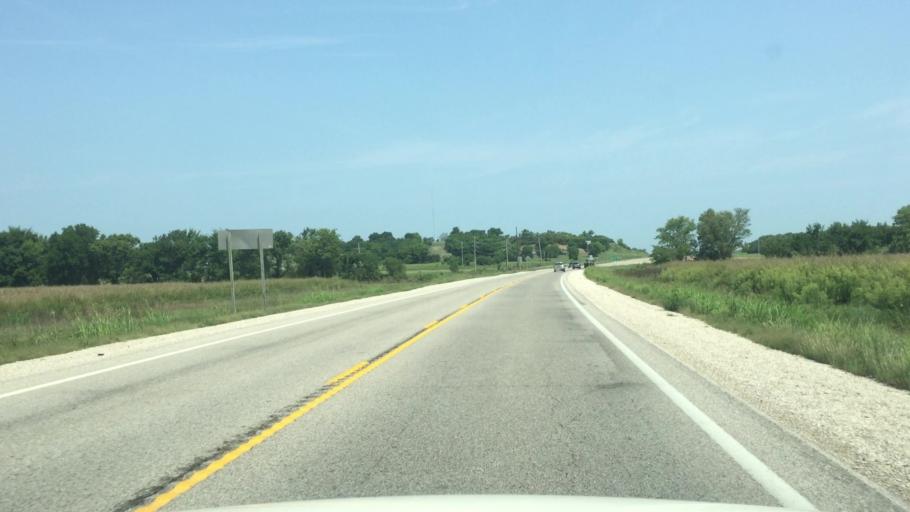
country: US
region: Kansas
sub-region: Montgomery County
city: Cherryvale
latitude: 37.2041
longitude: -95.5843
